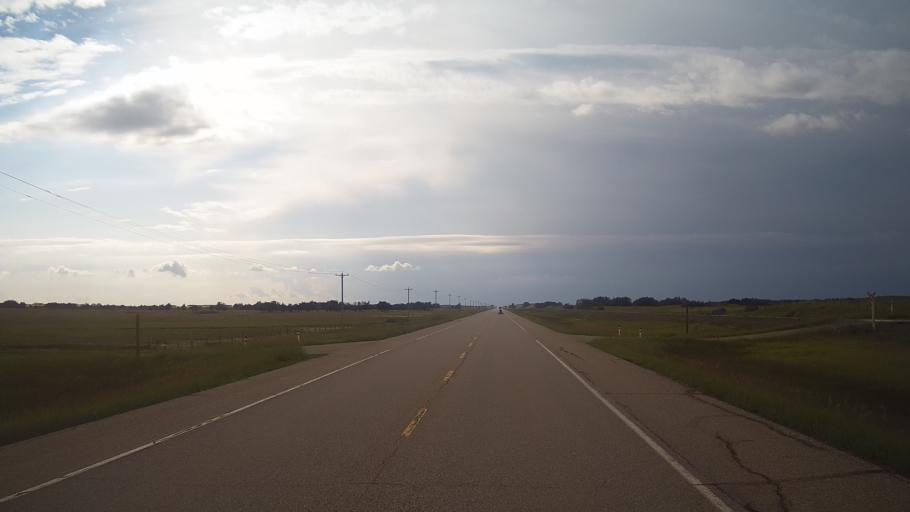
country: CA
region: Alberta
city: Viking
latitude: 53.1454
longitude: -111.9538
